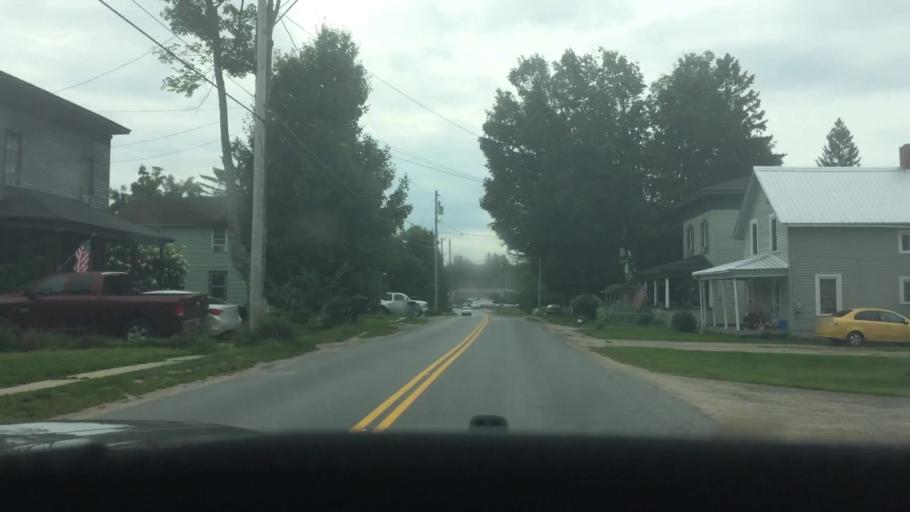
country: US
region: New York
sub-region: St. Lawrence County
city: Canton
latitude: 44.5070
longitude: -75.2757
